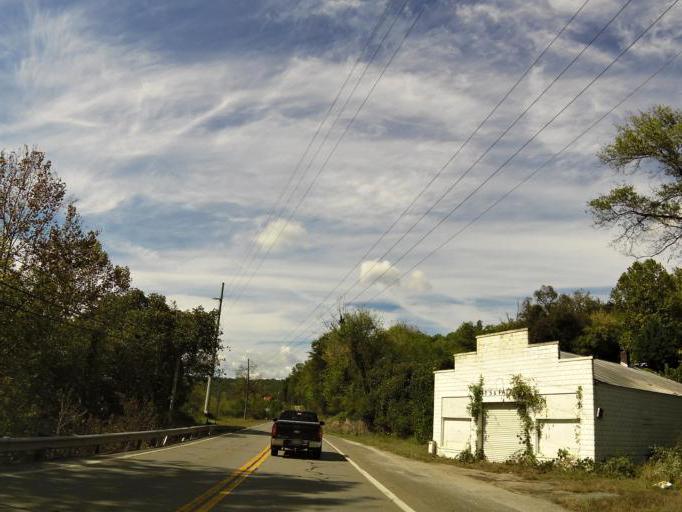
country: US
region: Georgia
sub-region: Pickens County
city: Nelson
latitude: 34.4320
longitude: -84.3387
